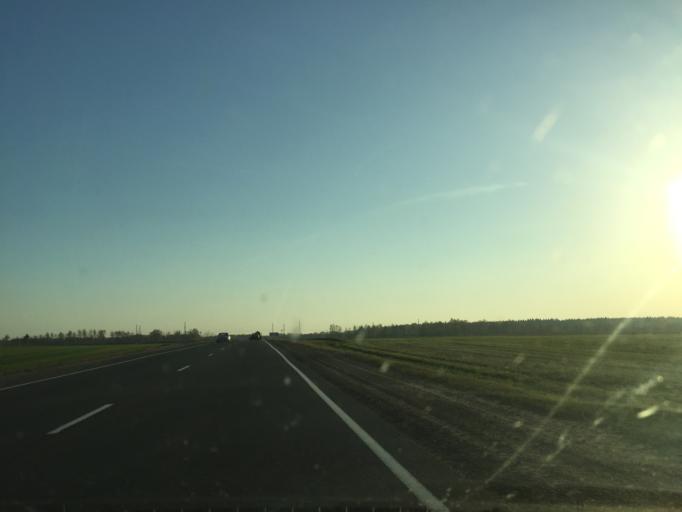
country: BY
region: Mogilev
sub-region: Mahilyowski Rayon
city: Kadino
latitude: 53.8722
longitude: 30.4851
